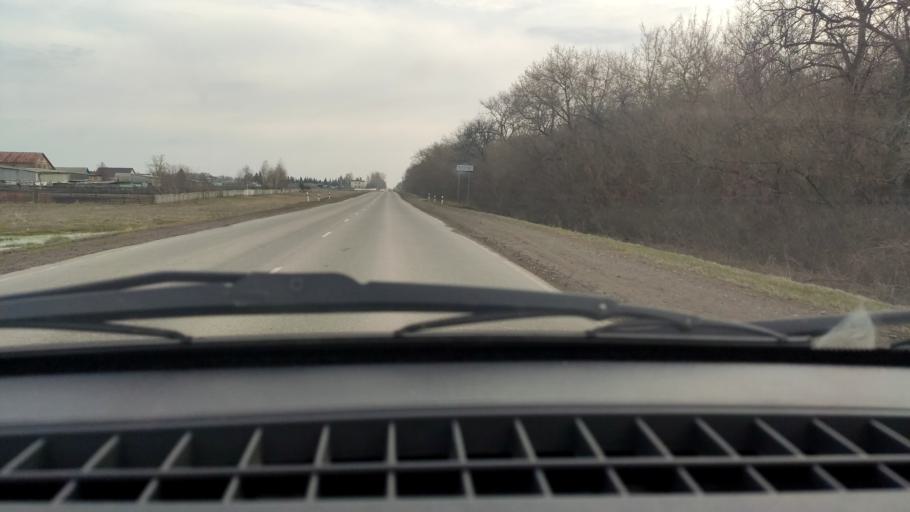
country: RU
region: Bashkortostan
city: Davlekanovo
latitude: 54.2887
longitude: 55.1183
